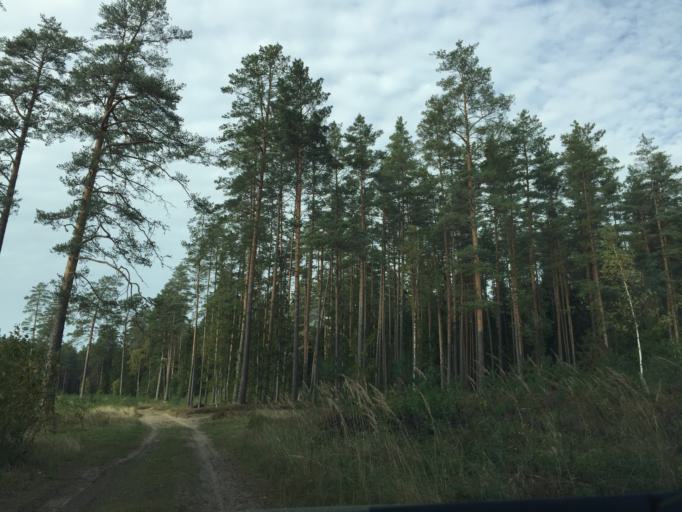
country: LV
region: Garkalne
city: Garkalne
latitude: 56.9455
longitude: 24.4330
